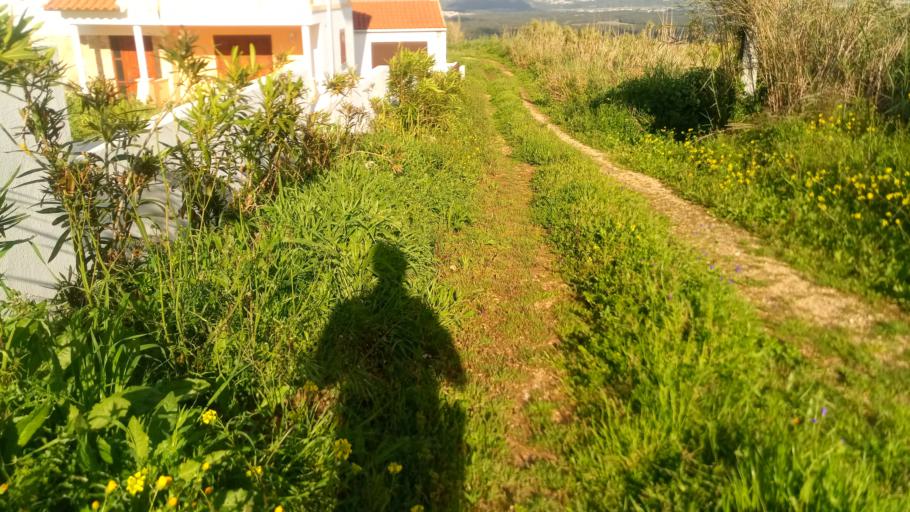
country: PT
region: Leiria
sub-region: Caldas da Rainha
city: Caldas da Rainha
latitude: 39.4559
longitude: -9.1964
